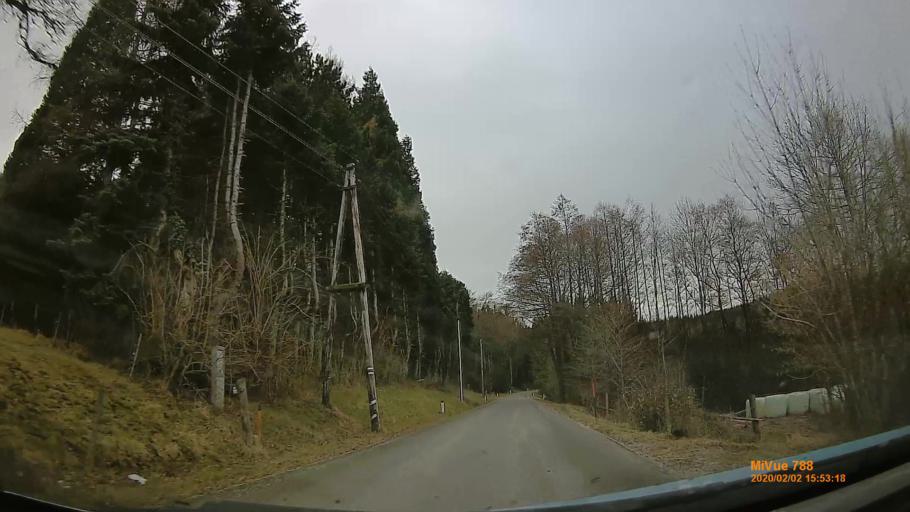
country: AT
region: Lower Austria
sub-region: Politischer Bezirk Neunkirchen
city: Reichenau an der Rax
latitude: 47.6743
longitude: 15.7998
